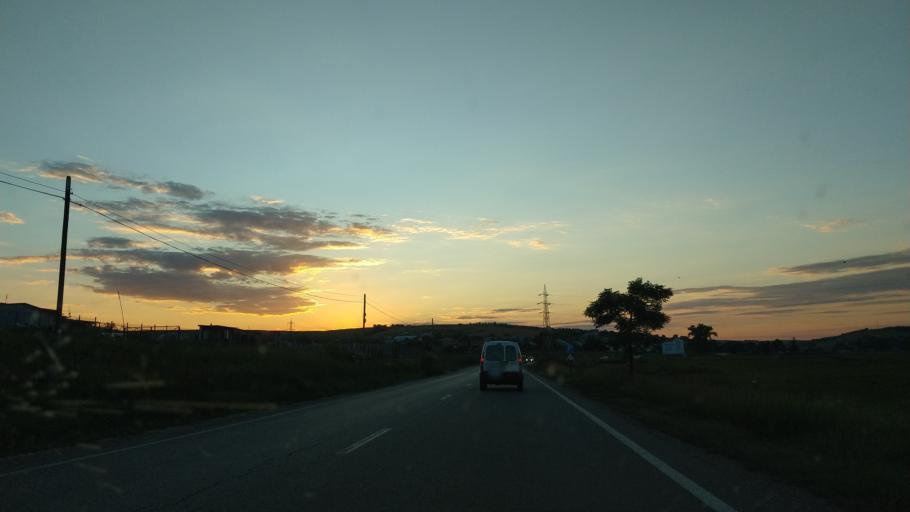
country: RO
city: Vanatori
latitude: 47.2272
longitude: 27.5396
